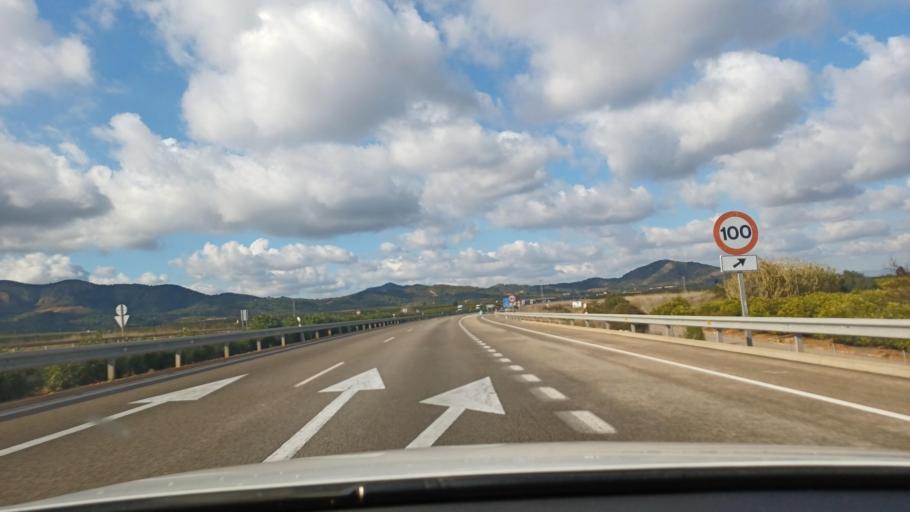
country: ES
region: Valencia
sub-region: Provincia de Castello
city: Villavieja
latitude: 39.8730
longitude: -0.1879
